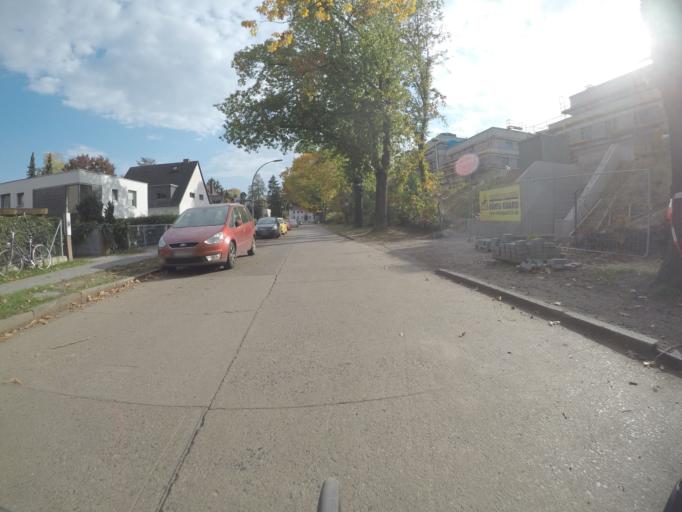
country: DE
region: Berlin
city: Hermsdorf
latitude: 52.6151
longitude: 13.3120
